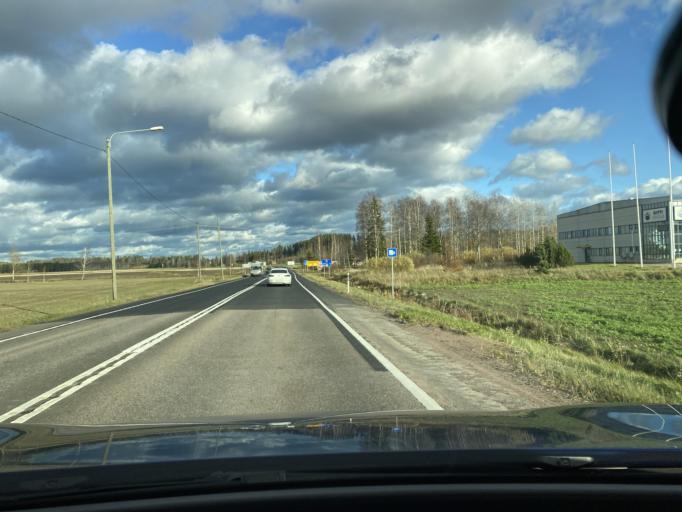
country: FI
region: Haeme
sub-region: Riihimaeki
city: Oitti
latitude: 60.7951
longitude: 25.0175
